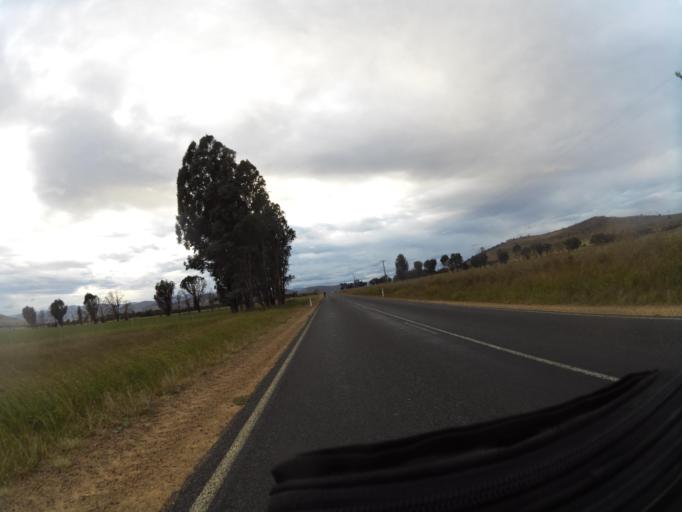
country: AU
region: New South Wales
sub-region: Greater Hume Shire
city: Holbrook
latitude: -36.0686
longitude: 147.9575
